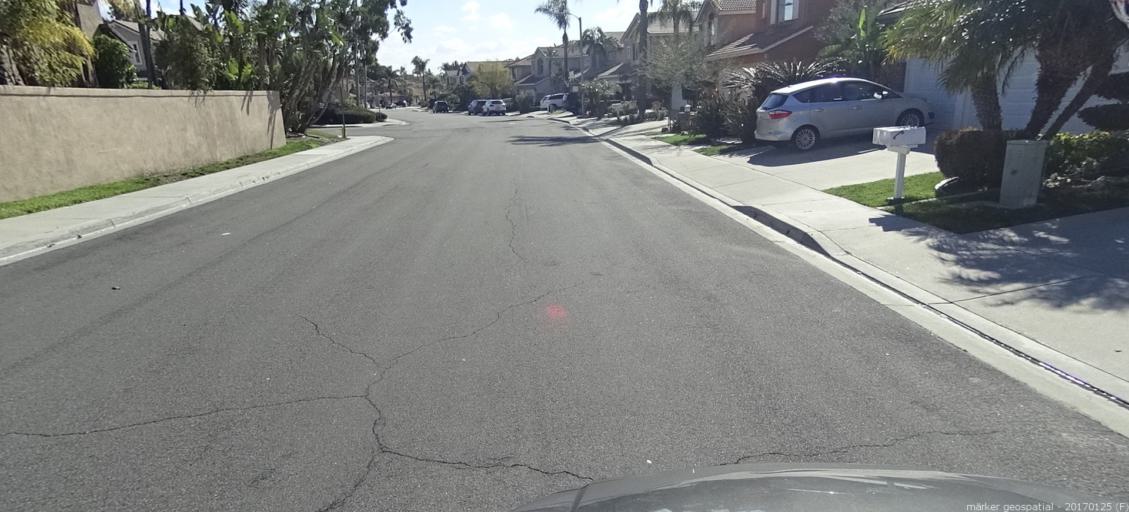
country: US
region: California
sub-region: Orange County
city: Foothill Ranch
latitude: 33.6899
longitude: -117.6557
